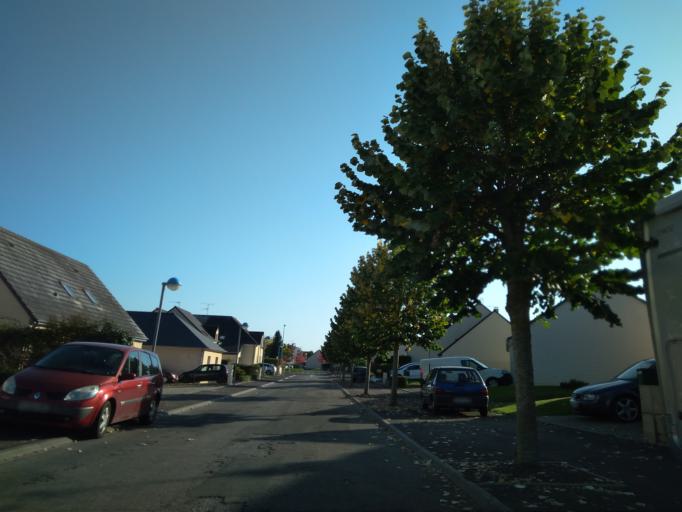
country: FR
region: Pays de la Loire
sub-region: Departement de la Mayenne
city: Louverne
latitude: 48.1149
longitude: -0.7170
